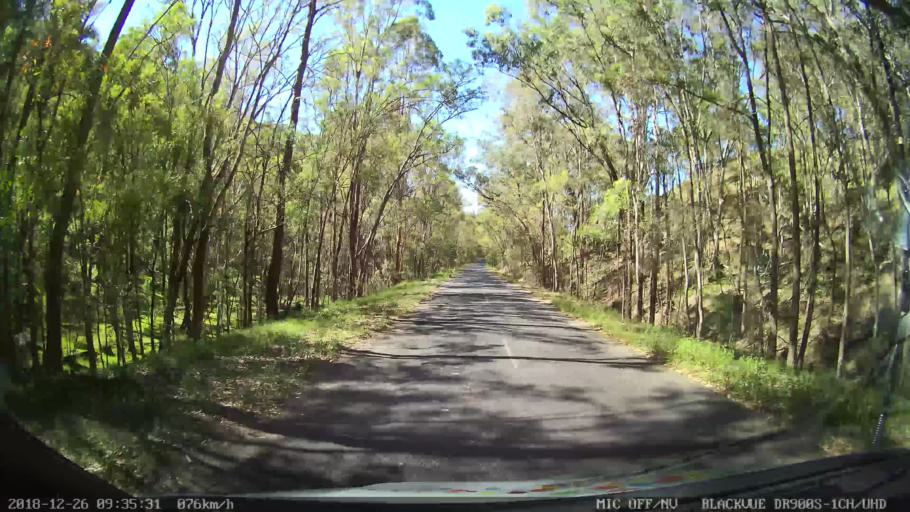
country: AU
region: New South Wales
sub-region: Mid-Western Regional
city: Kandos
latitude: -32.9152
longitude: 150.0413
